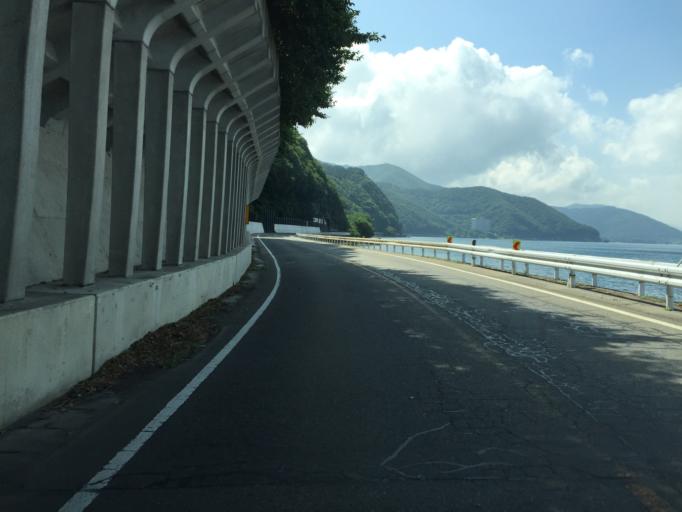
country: JP
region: Fukushima
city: Inawashiro
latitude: 37.4750
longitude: 140.1494
